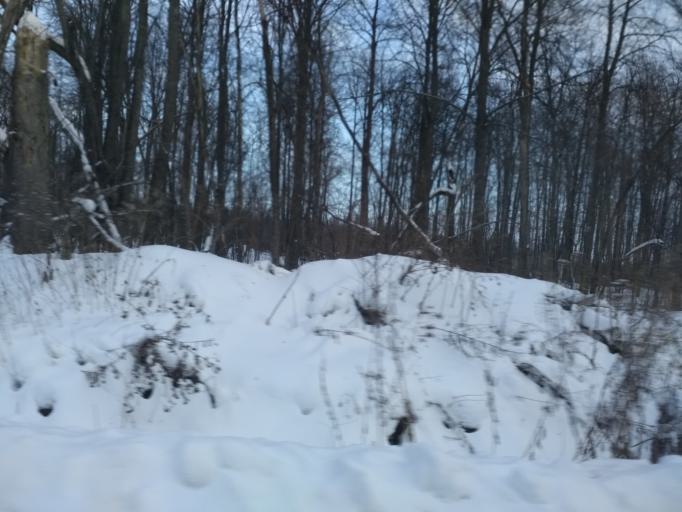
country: RU
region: Bashkortostan
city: Kudeyevskiy
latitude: 54.7119
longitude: 56.6470
